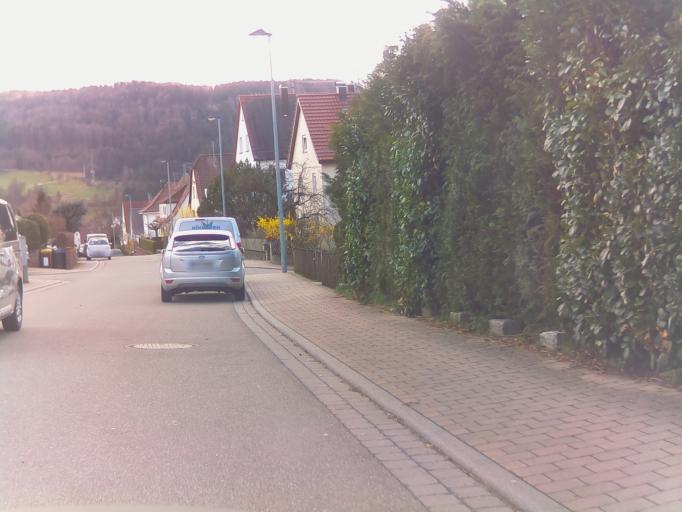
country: DE
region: Baden-Wuerttemberg
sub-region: Regierungsbezirk Stuttgart
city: Sulzbach an der Murr
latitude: 49.0079
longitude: 9.4970
